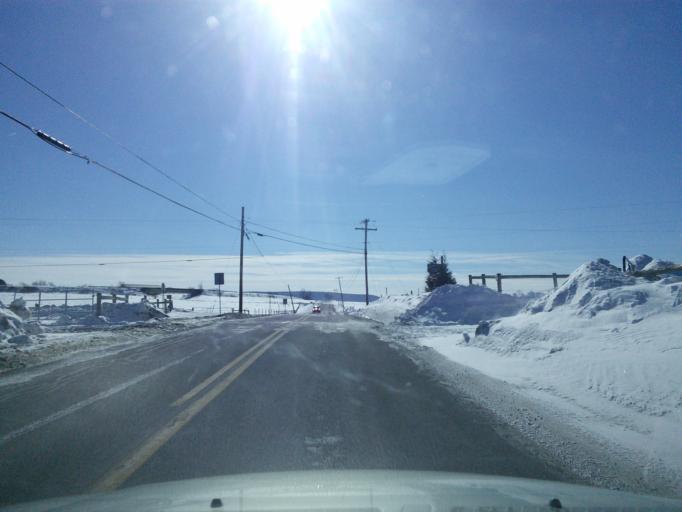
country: US
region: Pennsylvania
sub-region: Centre County
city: Houserville
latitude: 40.8666
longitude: -77.8407
